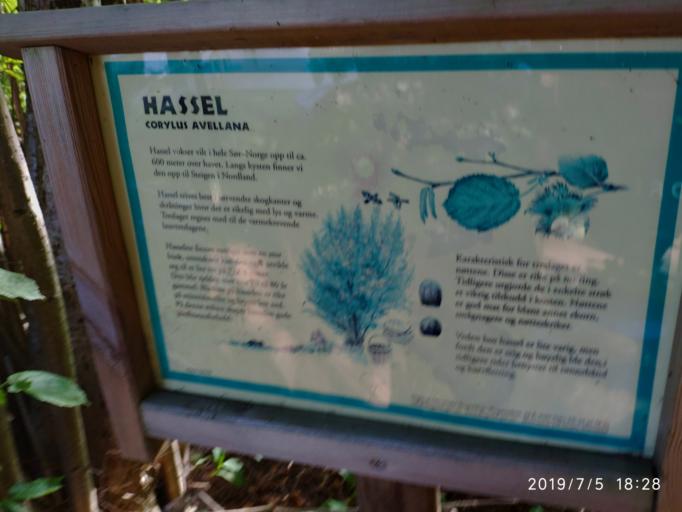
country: NO
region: Akershus
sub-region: Frogn
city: Drobak
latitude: 59.6717
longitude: 10.6442
